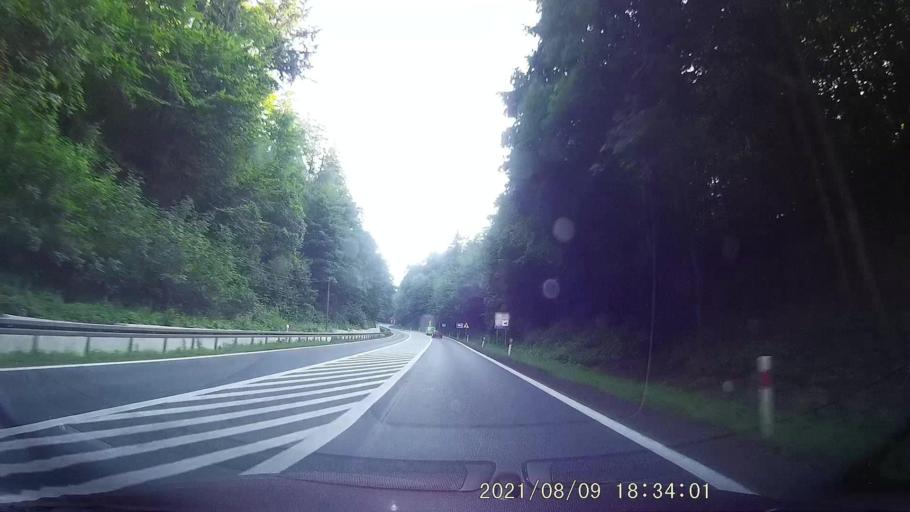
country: PL
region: Lower Silesian Voivodeship
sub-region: Powiat zabkowicki
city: Bardo
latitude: 50.4861
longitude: 16.7165
